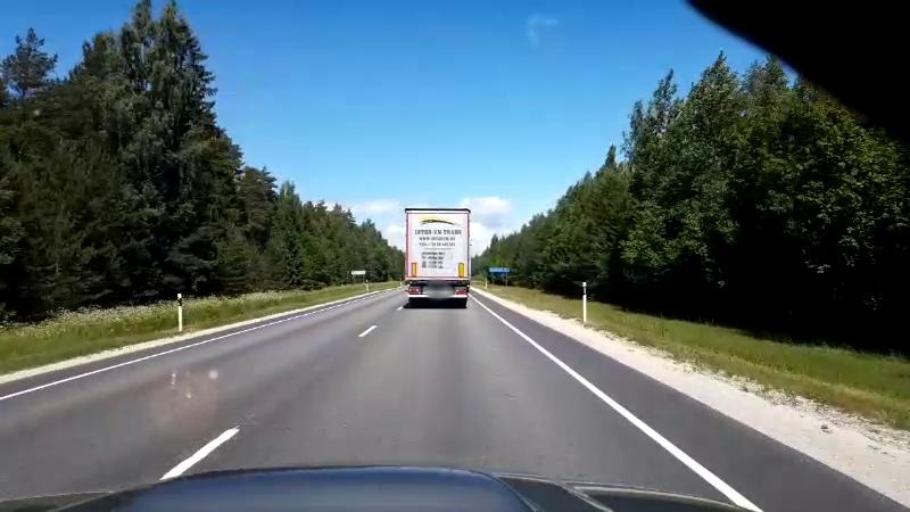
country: EE
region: Paernumaa
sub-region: Paernu linn
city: Parnu
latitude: 58.1121
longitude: 24.5097
